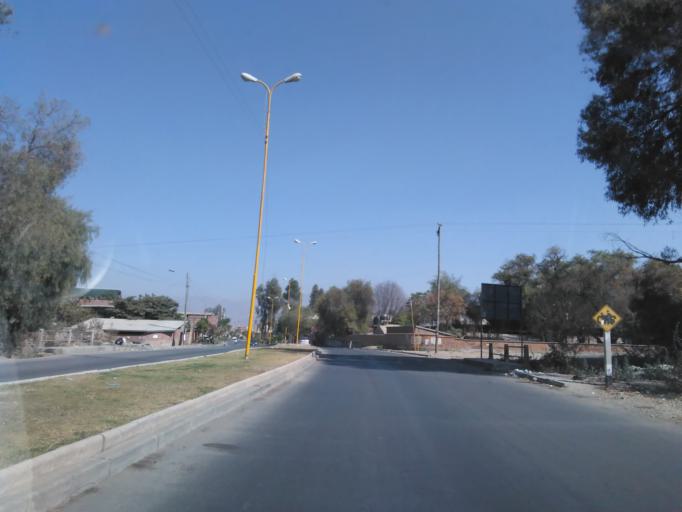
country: BO
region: Cochabamba
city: Cochabamba
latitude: -17.3937
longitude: -66.2678
